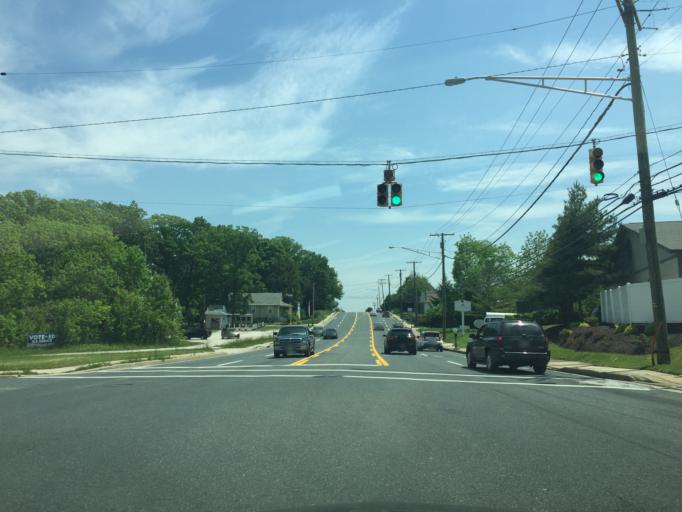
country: US
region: Maryland
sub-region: Baltimore County
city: Carney
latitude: 39.3950
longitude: -76.5126
